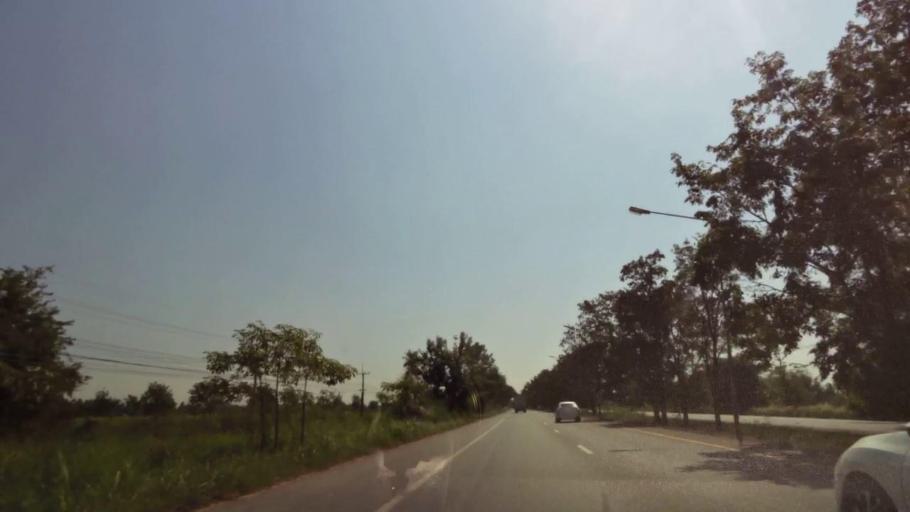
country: TH
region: Nakhon Sawan
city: Kao Liao
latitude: 15.9099
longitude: 100.1123
